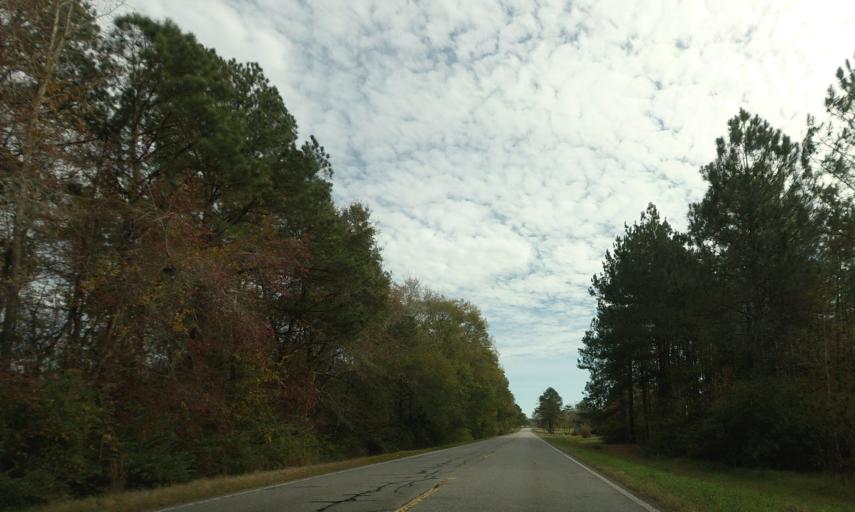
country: US
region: Georgia
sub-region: Bleckley County
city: Cochran
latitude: 32.3997
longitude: -83.2956
